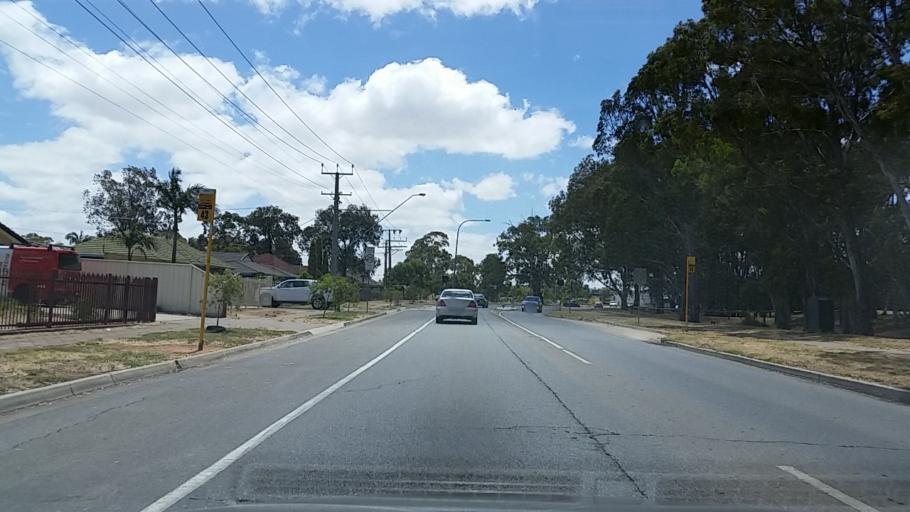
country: AU
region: South Australia
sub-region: Salisbury
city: Salisbury
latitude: -34.7695
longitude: 138.6192
